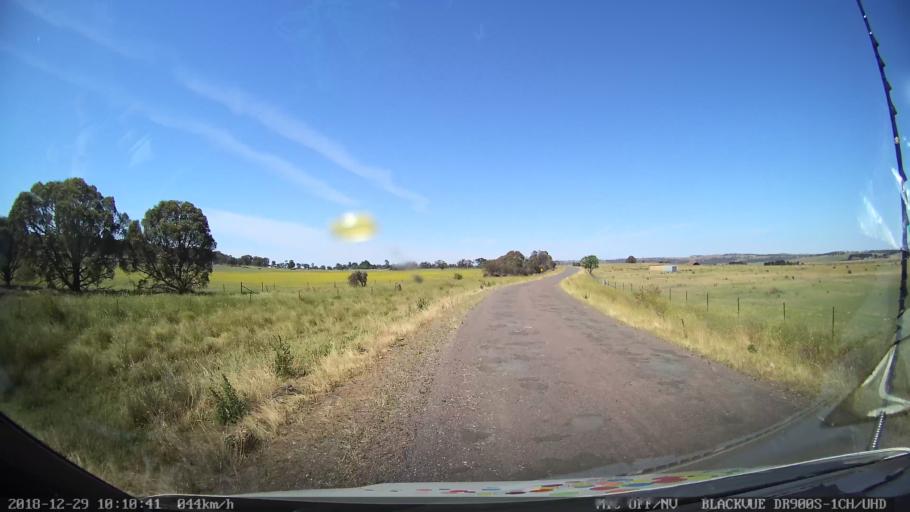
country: AU
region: New South Wales
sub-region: Yass Valley
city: Gundaroo
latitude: -34.8779
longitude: 149.4557
